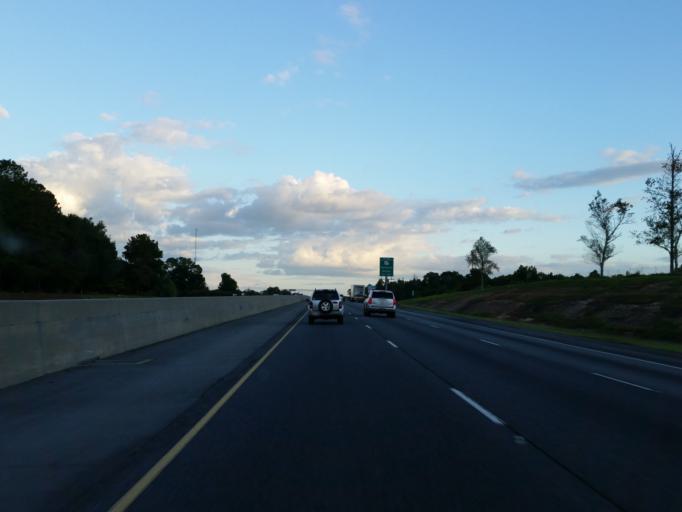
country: US
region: Georgia
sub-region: Turner County
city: Ashburn
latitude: 31.7516
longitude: -83.6639
